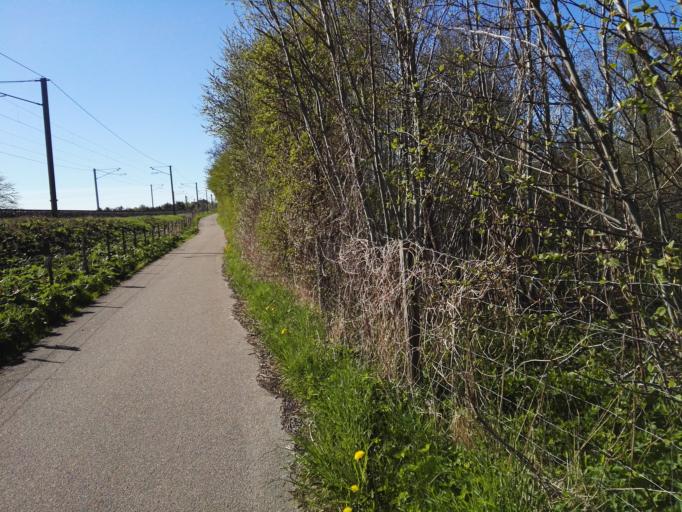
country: DK
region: Capital Region
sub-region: Egedal Kommune
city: Stenlose
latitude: 55.7550
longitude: 12.2091
